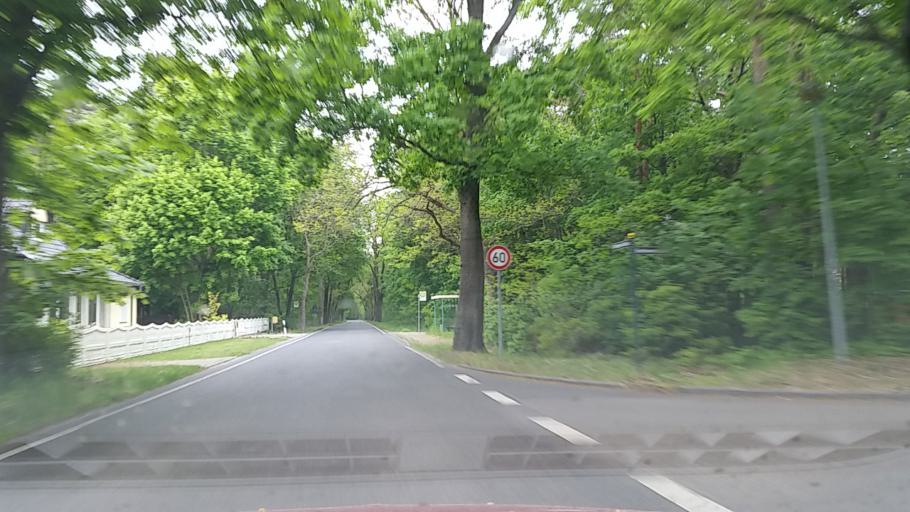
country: DE
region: Brandenburg
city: Diensdorf-Radlow
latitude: 52.2638
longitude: 14.0373
